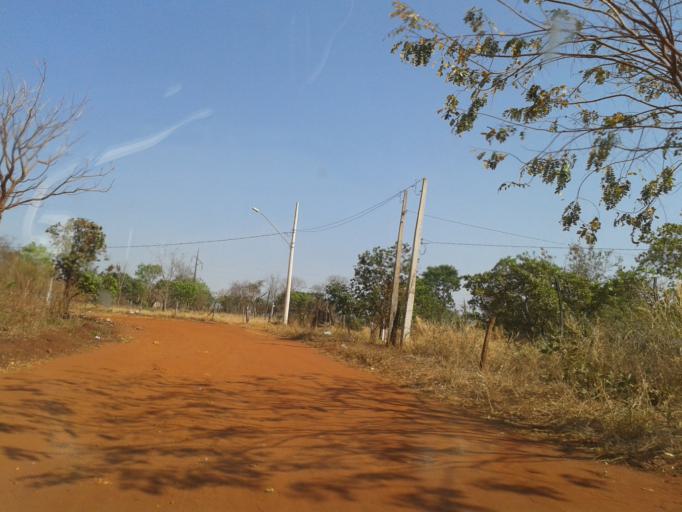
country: BR
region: Minas Gerais
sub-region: Ituiutaba
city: Ituiutaba
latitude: -18.9594
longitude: -49.4848
